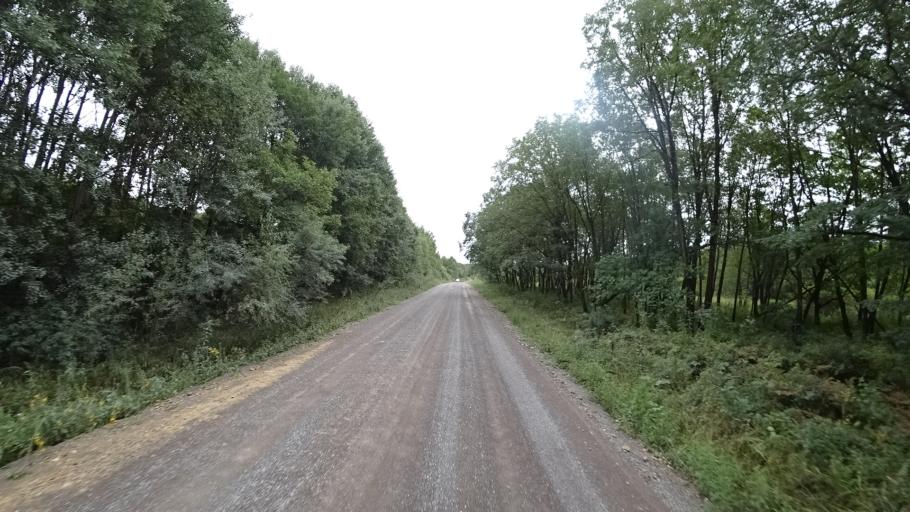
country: RU
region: Primorskiy
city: Ivanovka
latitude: 44.0434
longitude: 132.4939
